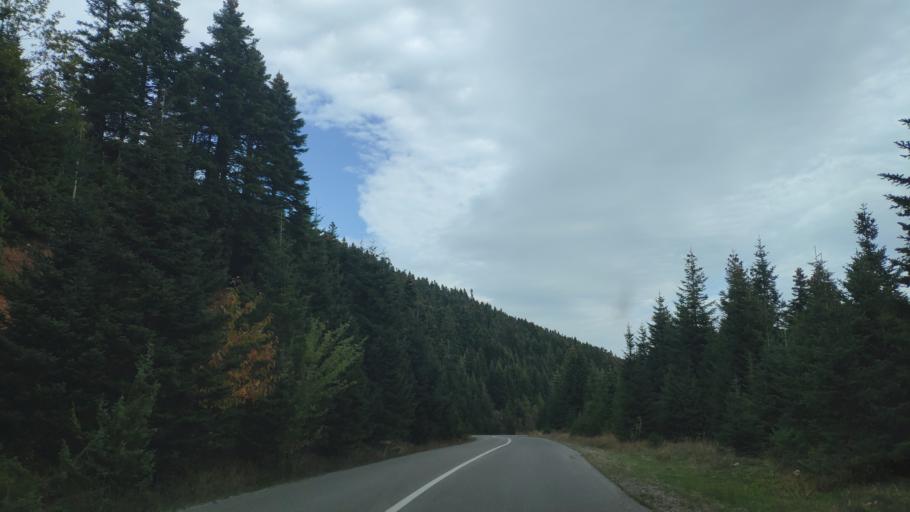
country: GR
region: Central Greece
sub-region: Nomos Fokidos
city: Amfissa
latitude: 38.7088
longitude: 22.3231
